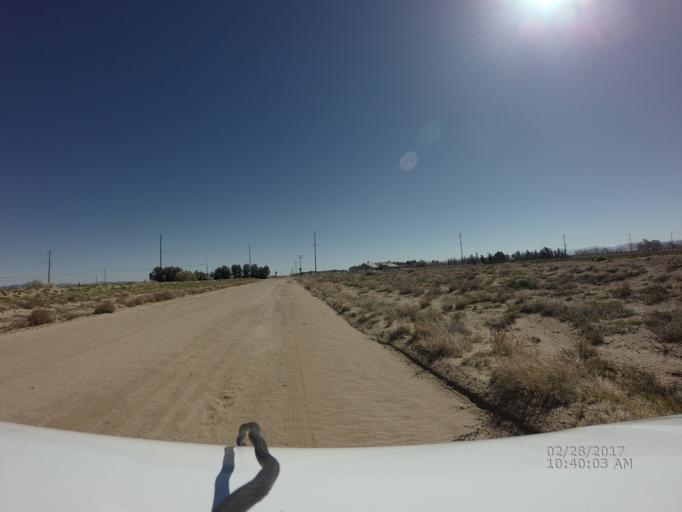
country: US
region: California
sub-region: Kern County
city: Rosamond
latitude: 34.7910
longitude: -118.2916
